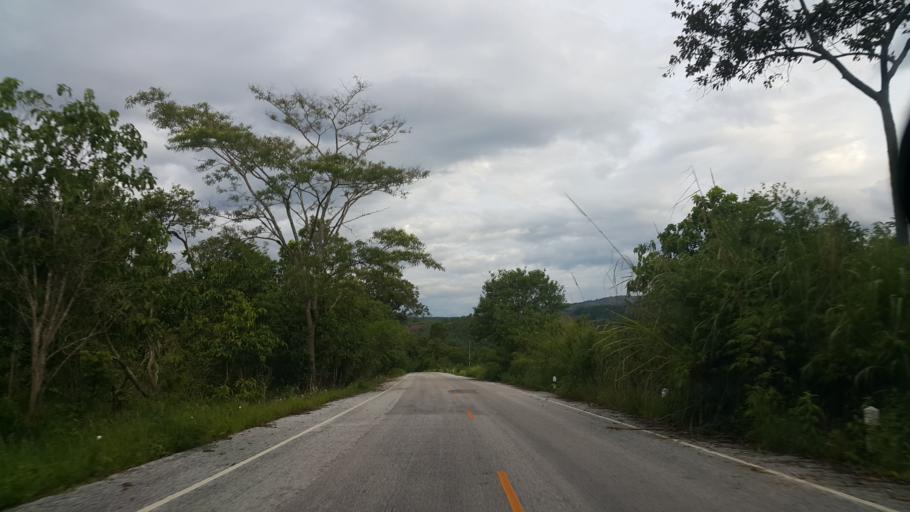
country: TH
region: Loei
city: Na Haeo
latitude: 17.4872
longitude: 101.1065
